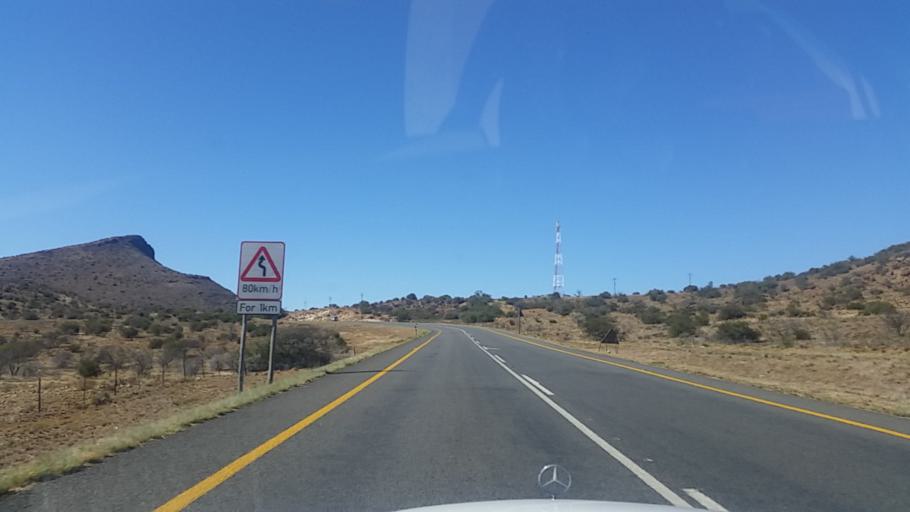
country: ZA
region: Eastern Cape
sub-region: Cacadu District Municipality
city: Graaff-Reinet
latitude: -32.1045
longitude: 24.6061
